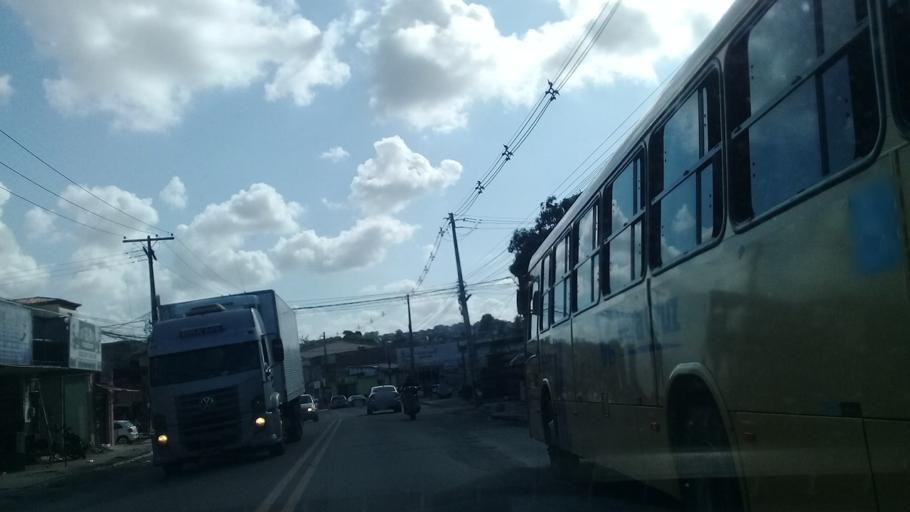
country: BR
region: Pernambuco
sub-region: Jaboatao Dos Guararapes
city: Jaboatao dos Guararapes
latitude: -8.1099
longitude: -34.9363
